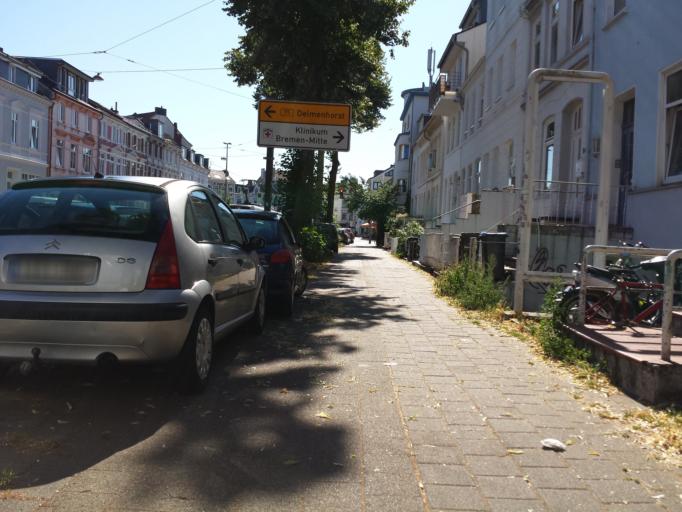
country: DE
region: Bremen
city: Bremen
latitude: 53.0714
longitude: 8.8352
